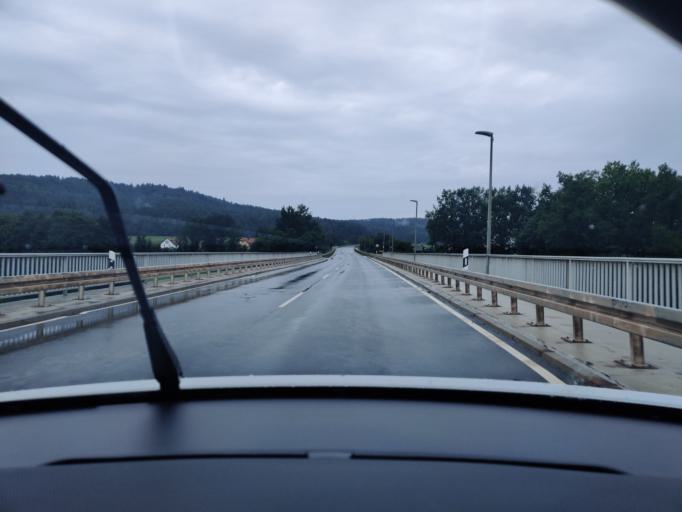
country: DE
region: Bavaria
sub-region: Upper Palatinate
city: Pfreimd
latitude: 49.4963
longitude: 12.1740
